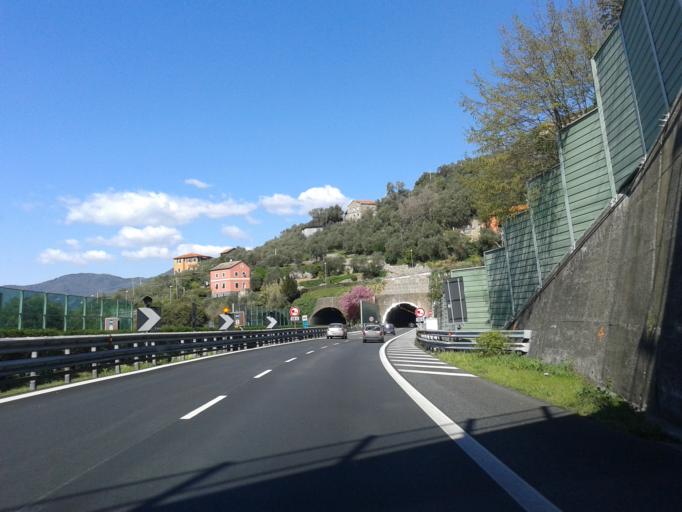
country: IT
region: Liguria
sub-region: Provincia di Genova
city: Rapallo
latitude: 44.3495
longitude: 9.2486
